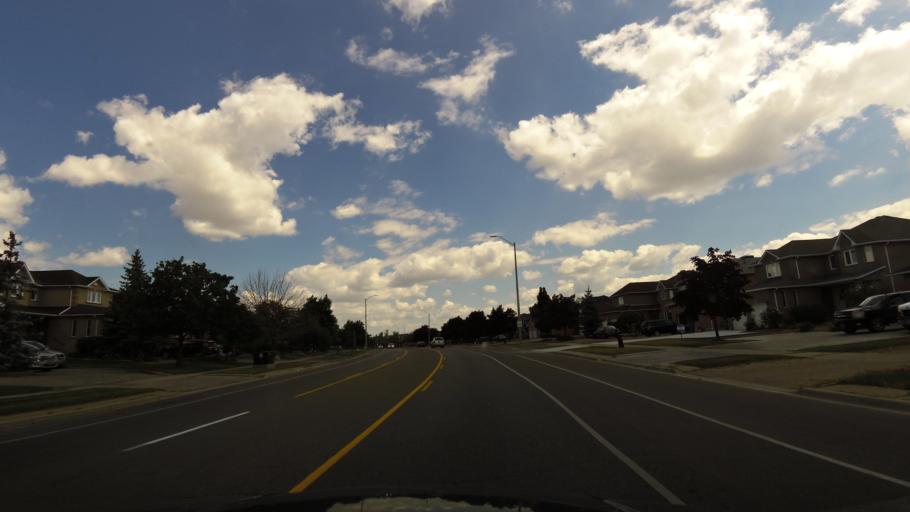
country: CA
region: Ontario
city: Mississauga
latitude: 43.6002
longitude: -79.6758
